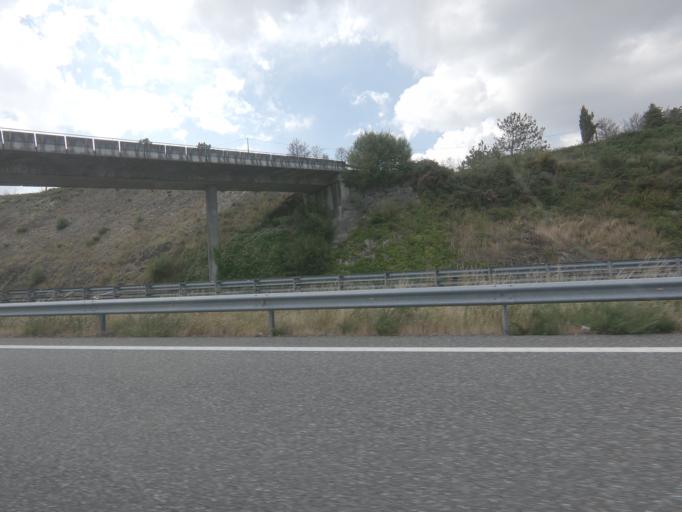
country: ES
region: Galicia
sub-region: Provincia de Ourense
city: Melon
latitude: 42.2595
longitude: -8.2169
